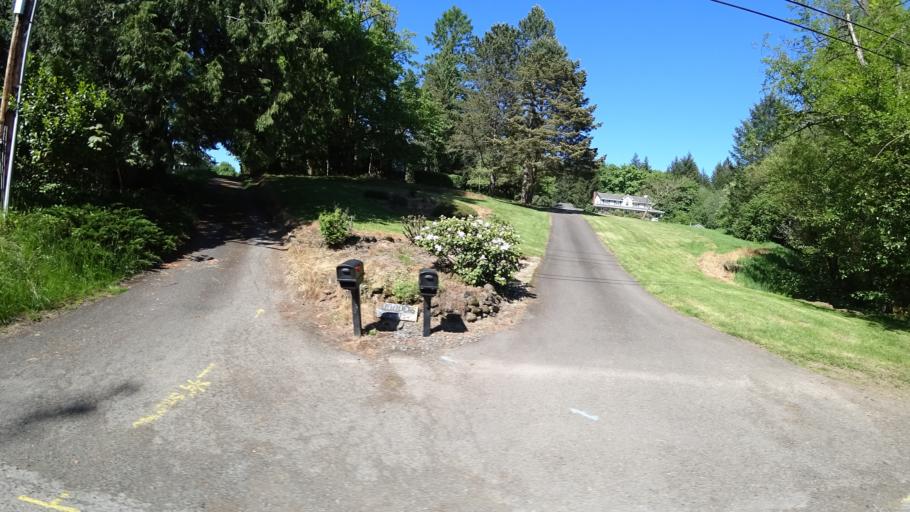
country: US
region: Oregon
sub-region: Washington County
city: Cedar Mill
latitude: 45.5545
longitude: -122.8031
